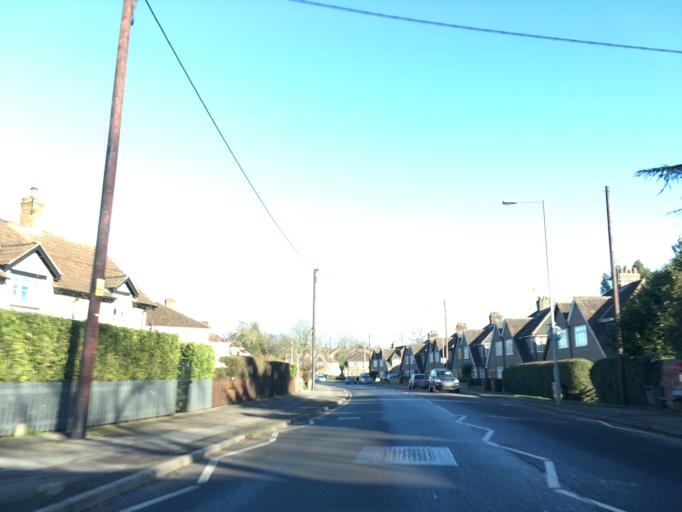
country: GB
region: England
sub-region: Wiltshire
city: Chippenham
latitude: 51.4660
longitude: -2.1151
